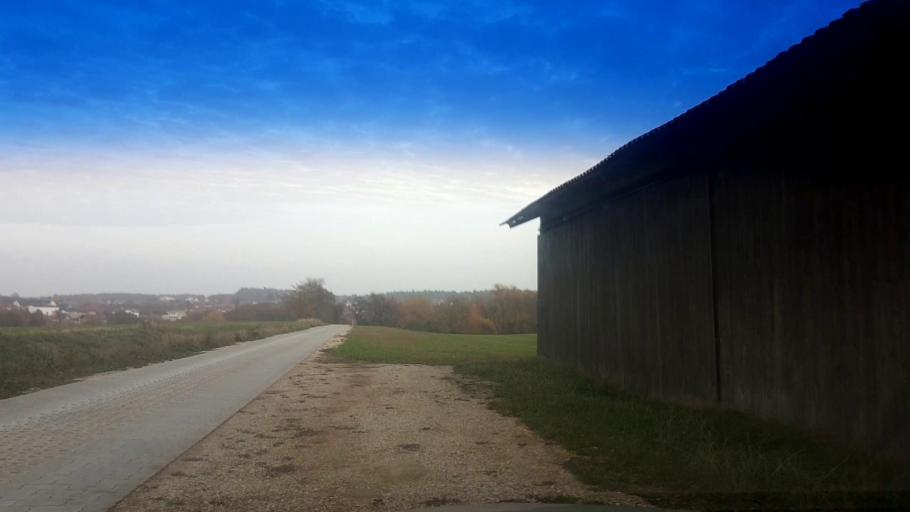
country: DE
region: Bavaria
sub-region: Upper Franconia
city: Viereth-Trunstadt
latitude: 49.9025
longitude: 10.7620
